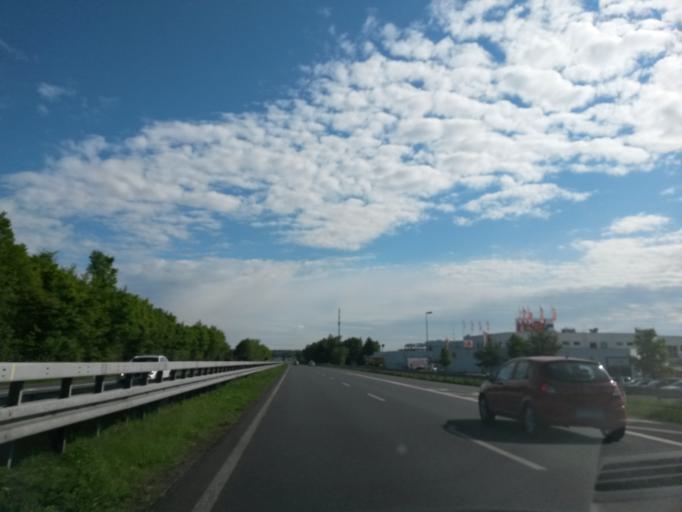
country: DE
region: Bavaria
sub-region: Regierungsbezirk Unterfranken
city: Wuerzburg
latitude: 49.8115
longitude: 9.9749
